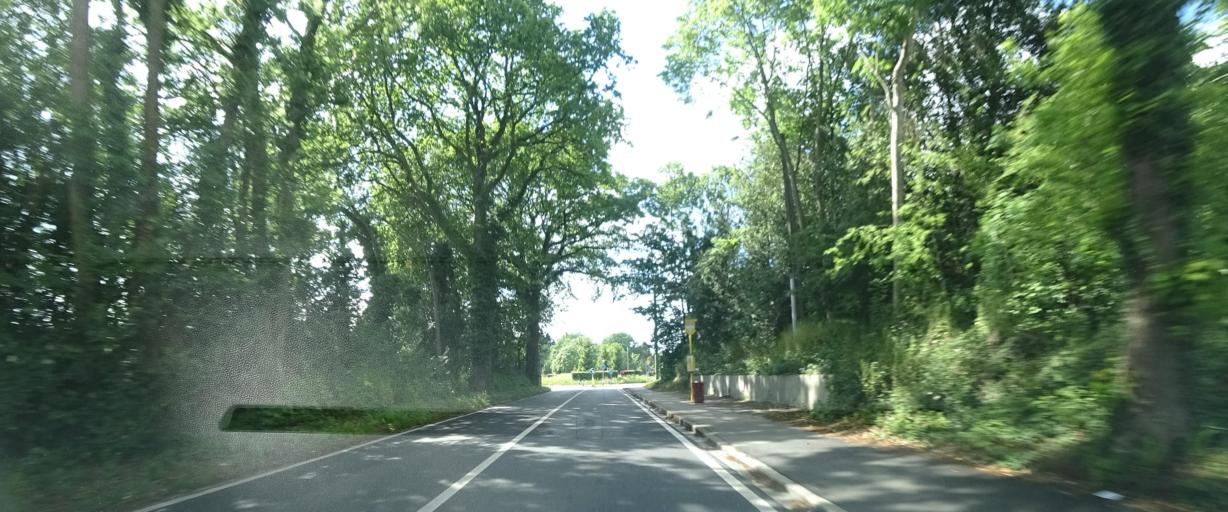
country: BE
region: Wallonia
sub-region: Province du Brabant Wallon
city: Wavre
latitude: 50.7049
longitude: 4.6305
